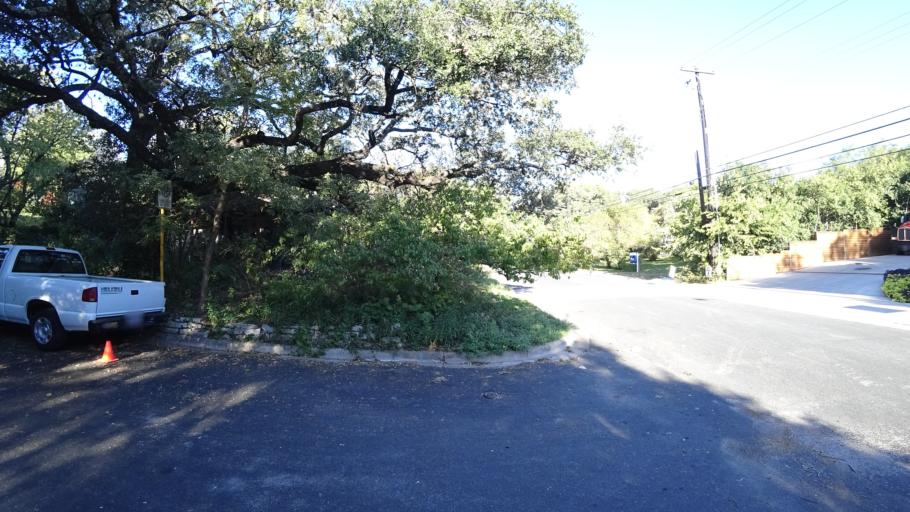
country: US
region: Texas
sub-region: Travis County
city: Austin
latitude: 30.2295
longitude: -97.7645
